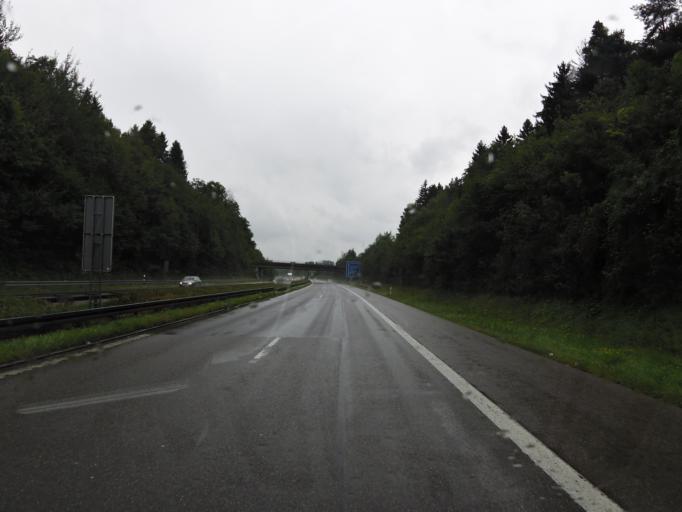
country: DE
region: Bavaria
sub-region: Swabia
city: Weissensberg
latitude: 47.5842
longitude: 9.7363
